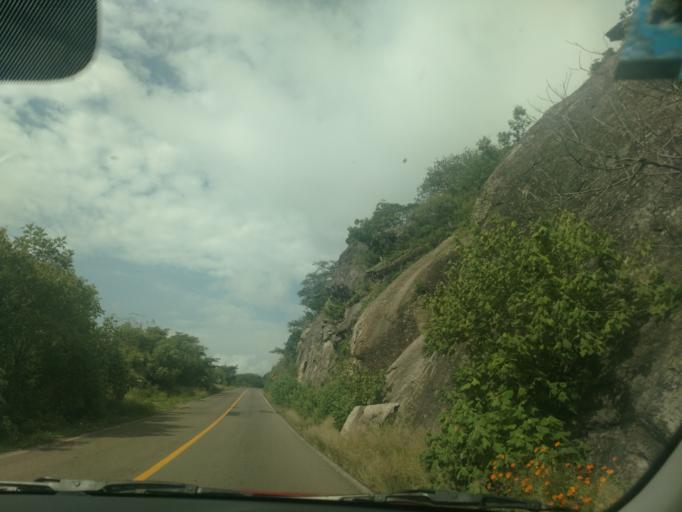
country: MX
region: Jalisco
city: El Salto
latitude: 20.3683
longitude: -104.5727
